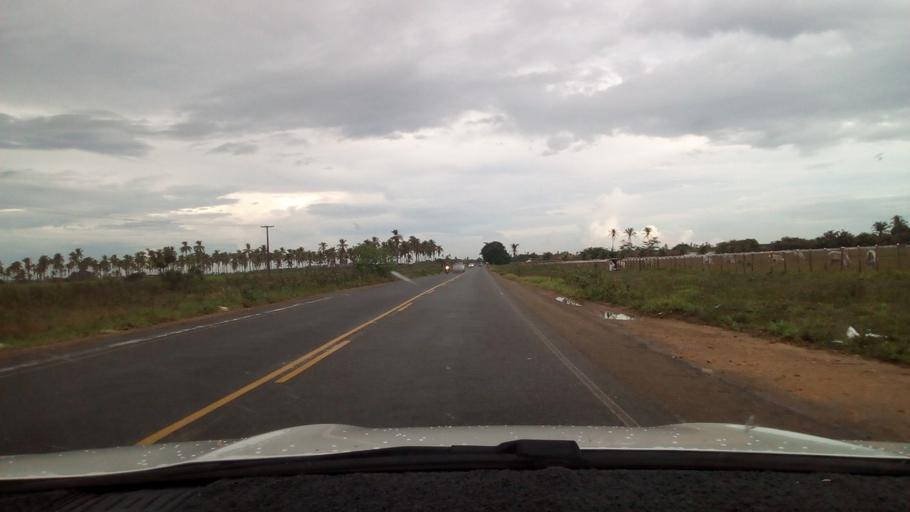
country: BR
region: Paraiba
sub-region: Mari
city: Mari
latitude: -7.0711
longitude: -35.2740
